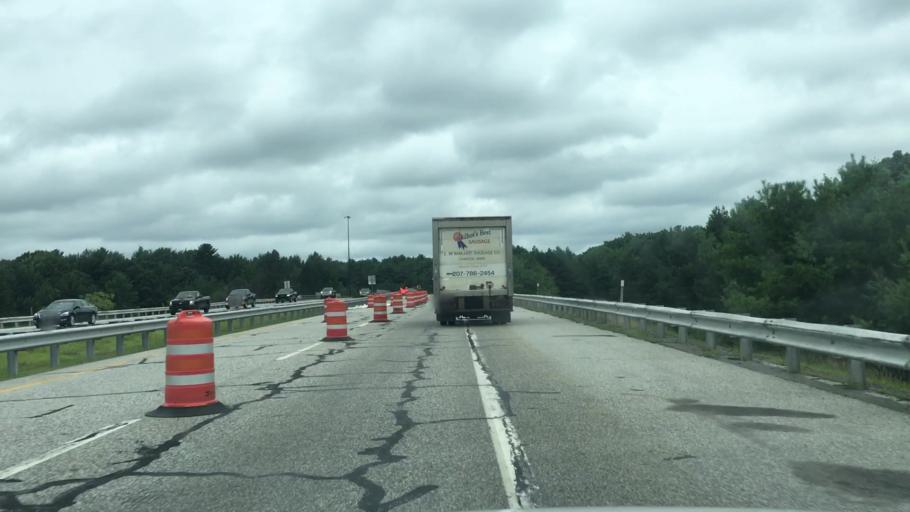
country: US
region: Maine
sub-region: York County
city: Saco
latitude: 43.5267
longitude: -70.4509
